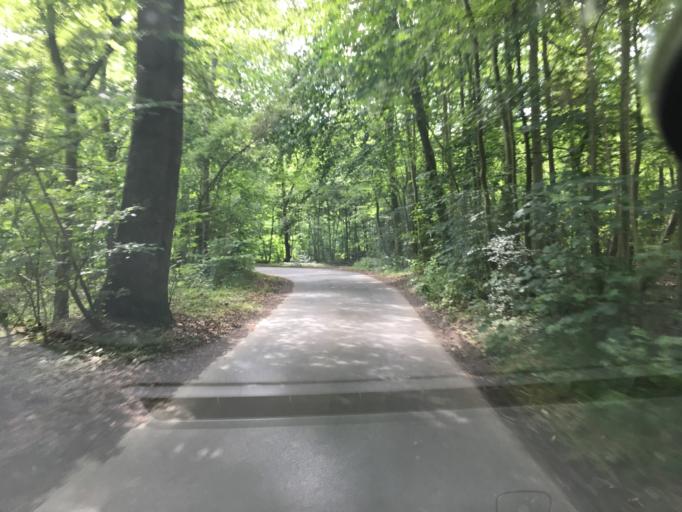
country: DK
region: South Denmark
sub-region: Sonderborg Kommune
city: Dybbol
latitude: 54.9369
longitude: 9.7393
